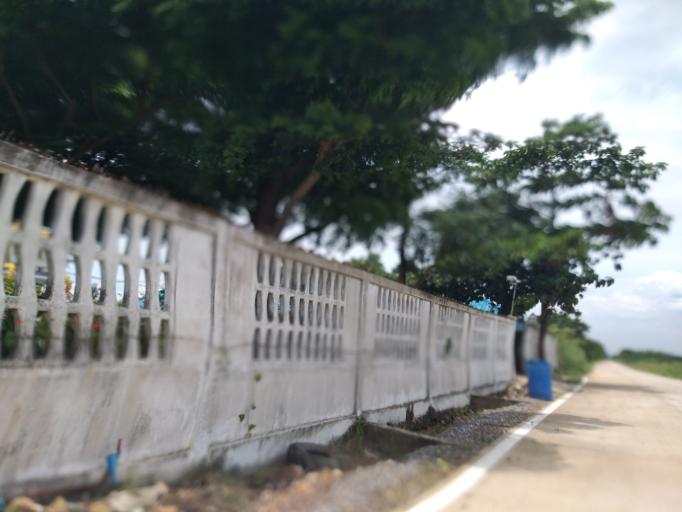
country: TH
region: Pathum Thani
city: Ban Lam Luk Ka
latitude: 13.9795
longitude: 100.8531
